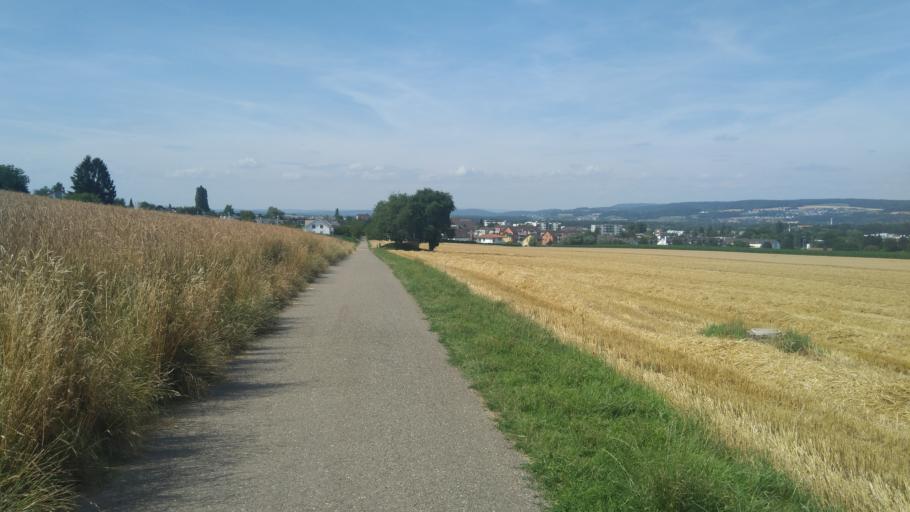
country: CH
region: Zurich
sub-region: Bezirk Dielsdorf
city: Ruemlang / Ruemlang (Dorfkern)
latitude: 47.4398
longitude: 8.5295
